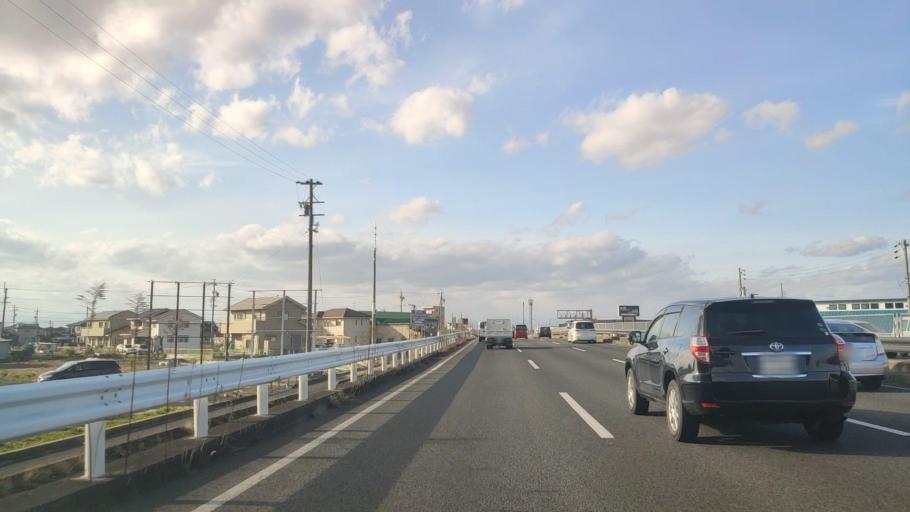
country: JP
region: Aichi
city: Kuroda
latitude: 35.3534
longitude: 136.7892
